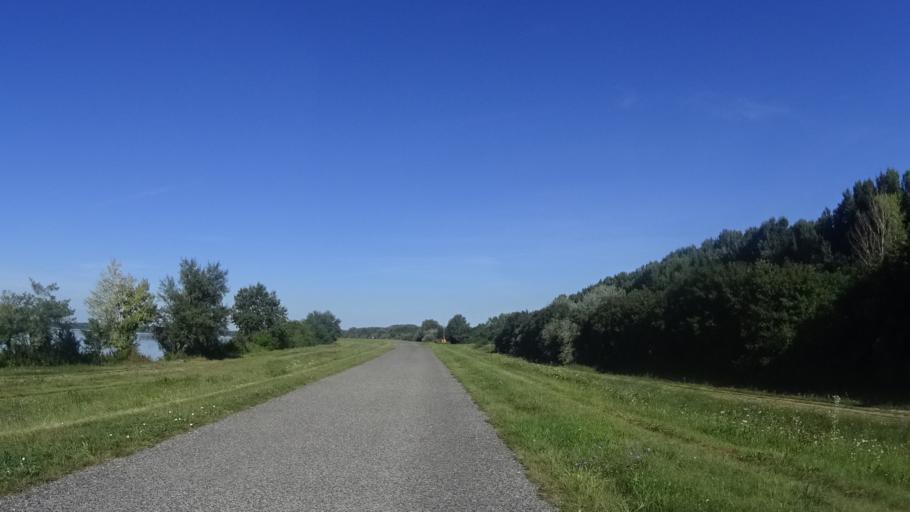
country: SK
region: Bratislavsky
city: Dunajska Luzna
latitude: 48.0578
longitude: 17.2241
